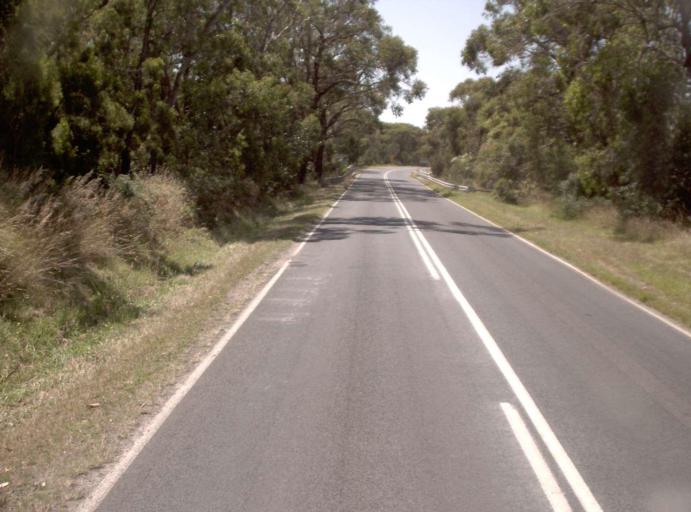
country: AU
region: Victoria
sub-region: Bass Coast
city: North Wonthaggi
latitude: -38.6264
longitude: 145.7540
